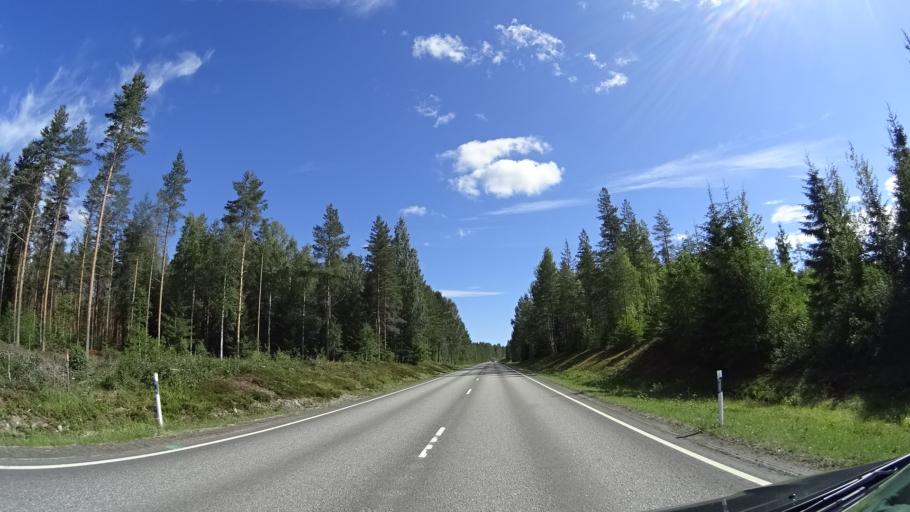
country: FI
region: Pirkanmaa
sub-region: Luoteis-Pirkanmaa
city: Kihnioe
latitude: 62.2147
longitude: 23.2545
